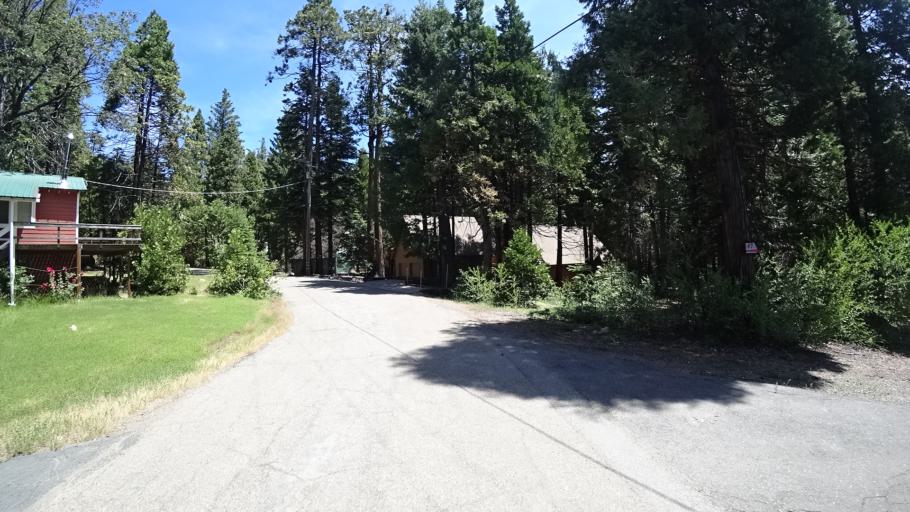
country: US
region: California
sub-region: Calaveras County
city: Arnold
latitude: 38.3564
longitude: -120.2115
